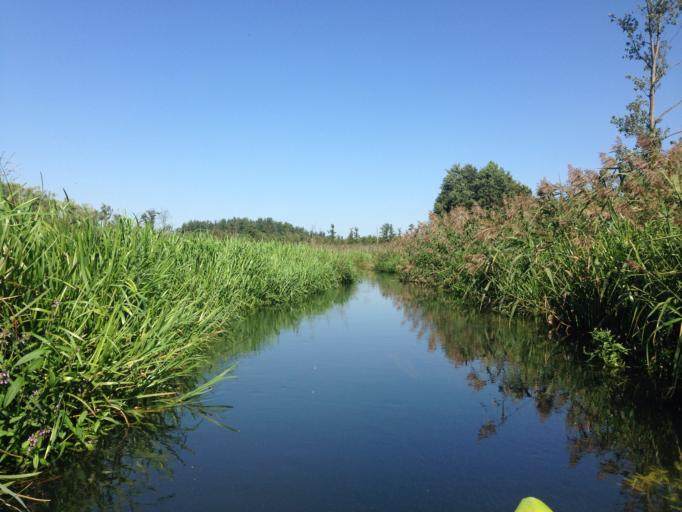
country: PL
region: Kujawsko-Pomorskie
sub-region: Powiat brodnicki
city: Bartniczka
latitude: 53.2564
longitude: 19.6020
